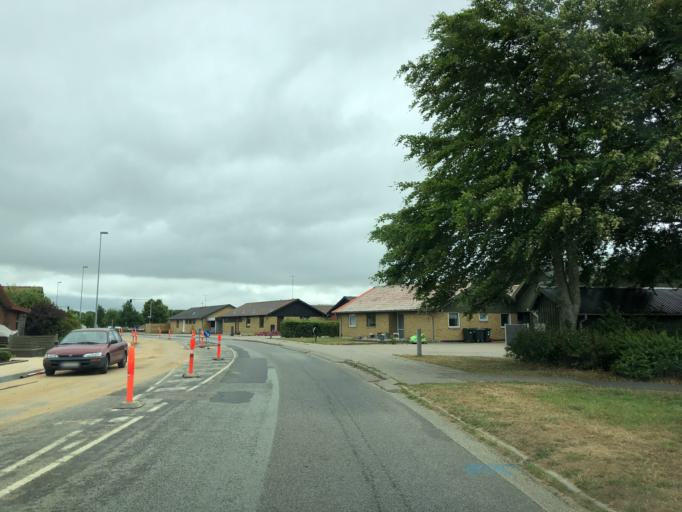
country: DK
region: Central Jutland
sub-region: Herning Kommune
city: Vildbjerg
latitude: 56.1942
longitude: 8.7597
